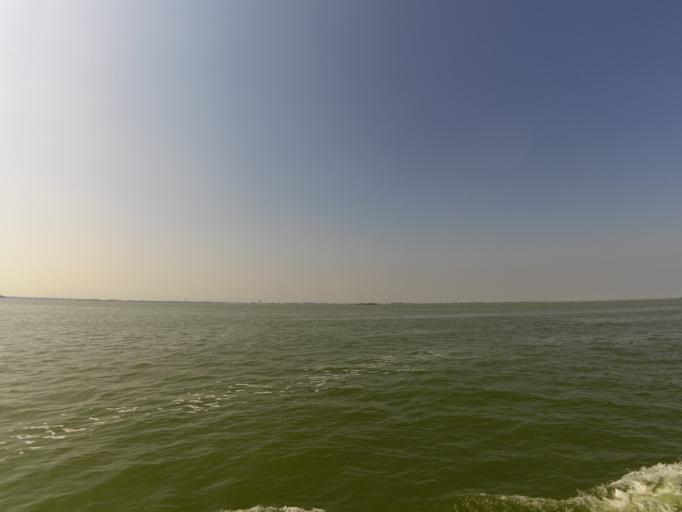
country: IT
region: Veneto
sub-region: Provincia di Venezia
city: Murano
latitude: 45.4730
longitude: 12.3852
